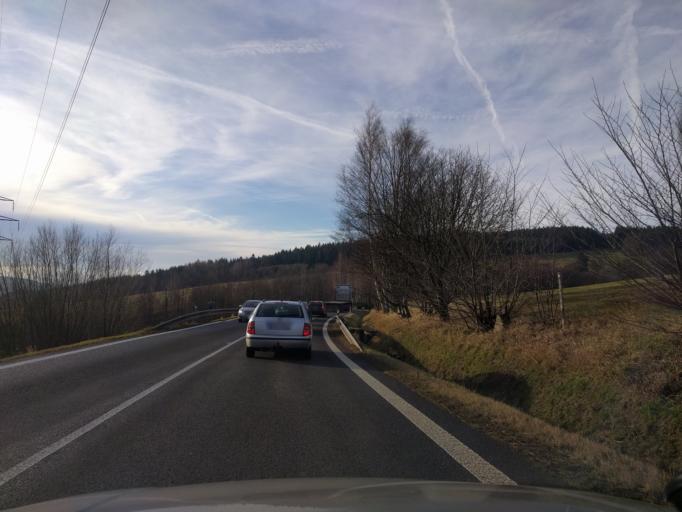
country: CZ
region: Liberecky
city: Mnisek
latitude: 50.8582
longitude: 15.0311
